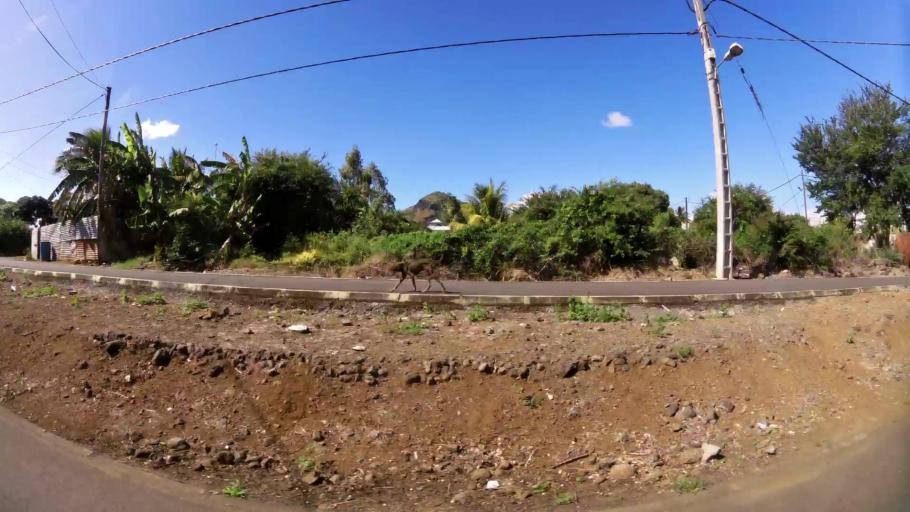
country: MU
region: Black River
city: Cascavelle
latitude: -20.2631
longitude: 57.4103
